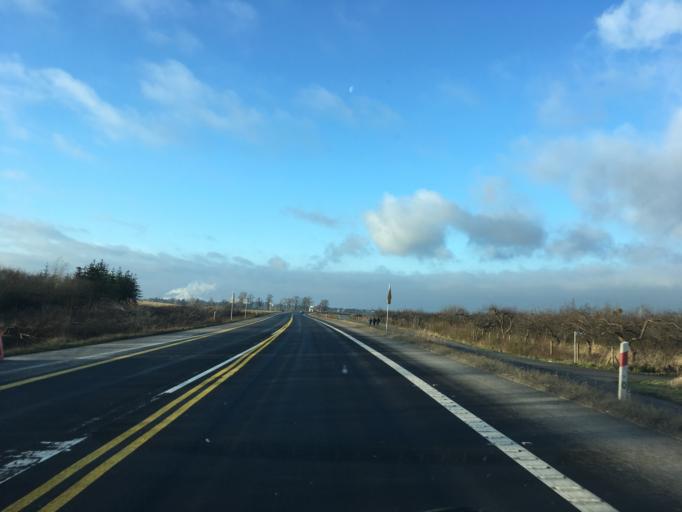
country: PL
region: Kujawsko-Pomorskie
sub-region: Powiat swiecki
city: Swiecie
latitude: 53.4205
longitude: 18.4627
